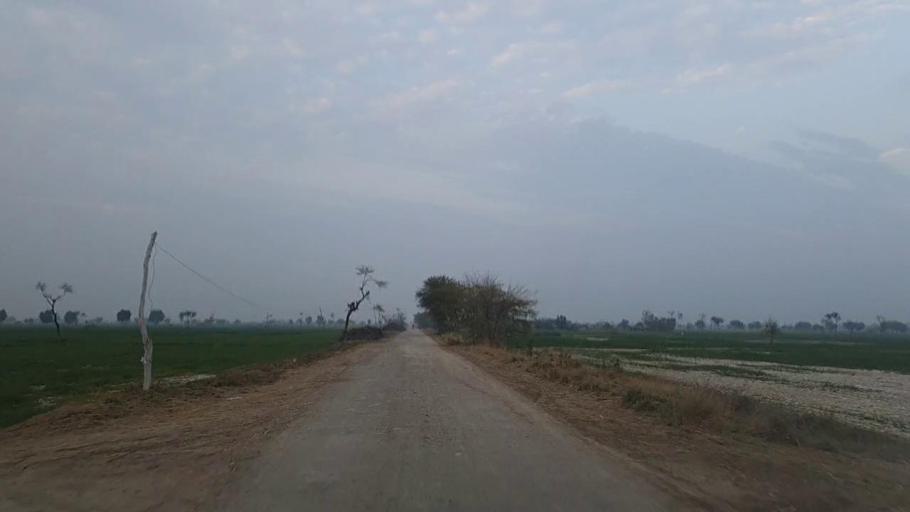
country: PK
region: Sindh
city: Jam Sahib
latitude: 26.3032
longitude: 68.5936
